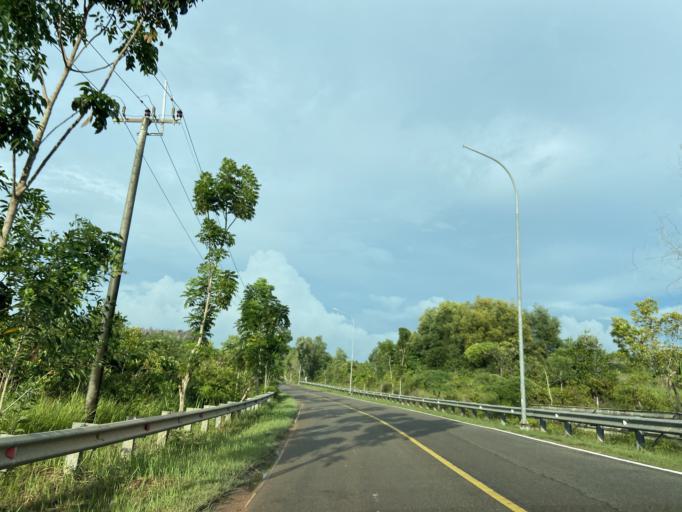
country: ID
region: Riau Islands
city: Tanjungpinang
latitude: 0.9500
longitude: 104.0669
